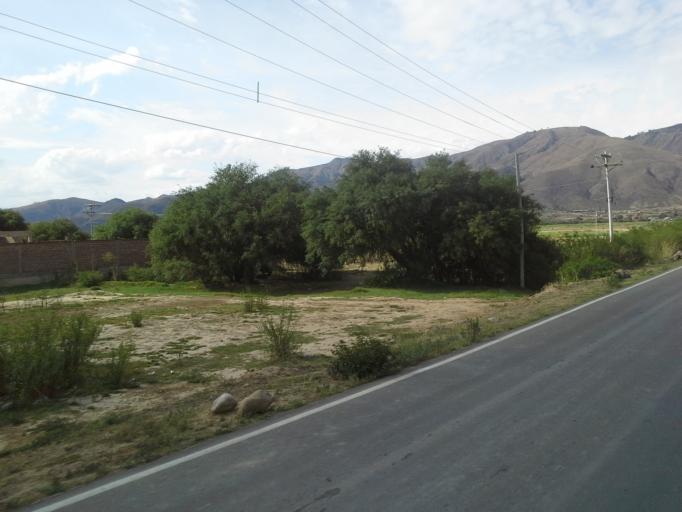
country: BO
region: Cochabamba
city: Tarata
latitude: -17.5610
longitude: -66.0089
